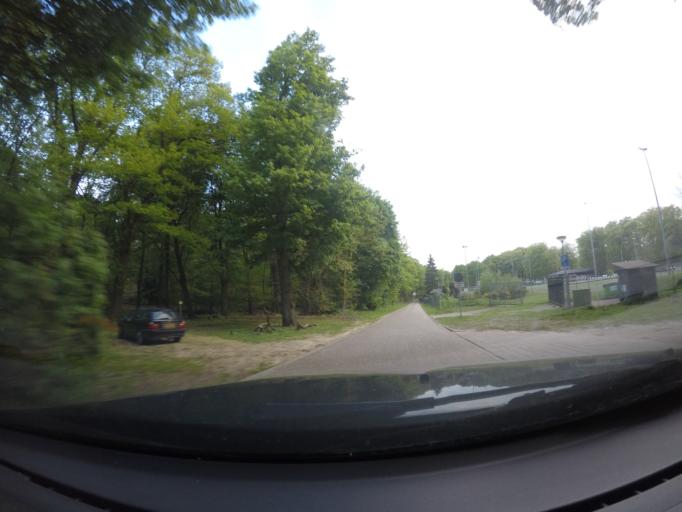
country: NL
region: Gelderland
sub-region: Gemeente Rozendaal
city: Rozendaal
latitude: 52.0106
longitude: 5.9773
